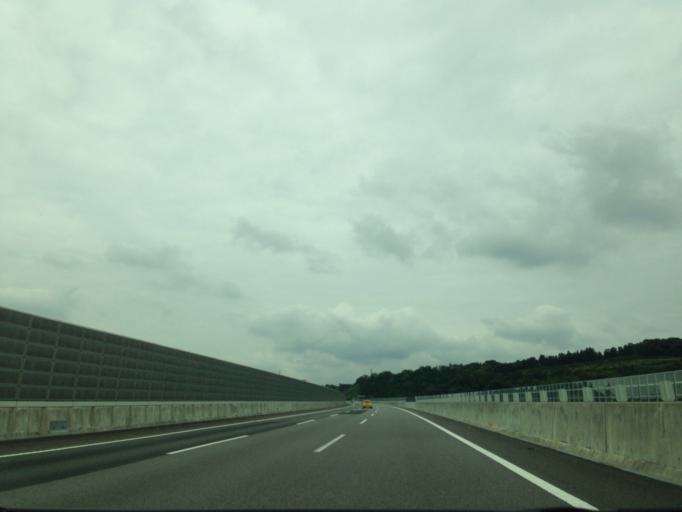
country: JP
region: Shizuoka
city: Hamakita
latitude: 34.8391
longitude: 137.7935
